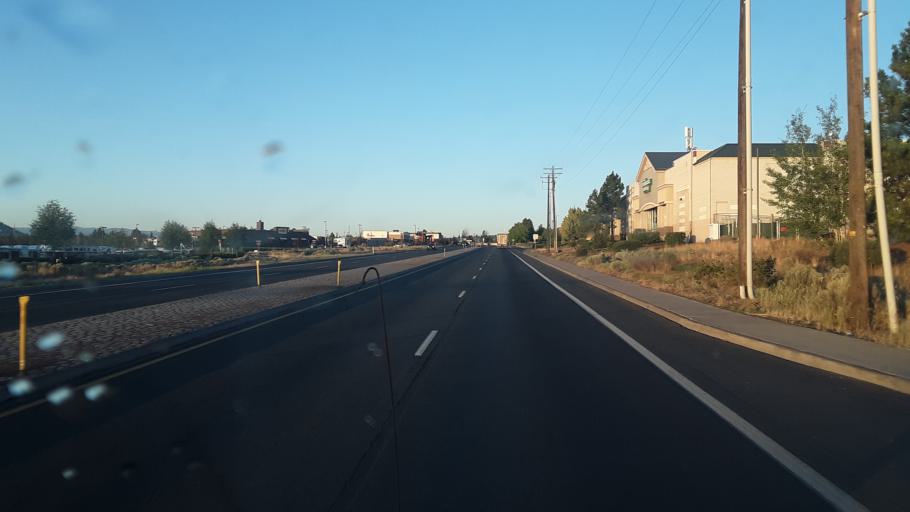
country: US
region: Oregon
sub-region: Deschutes County
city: Bend
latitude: 44.1069
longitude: -121.2967
